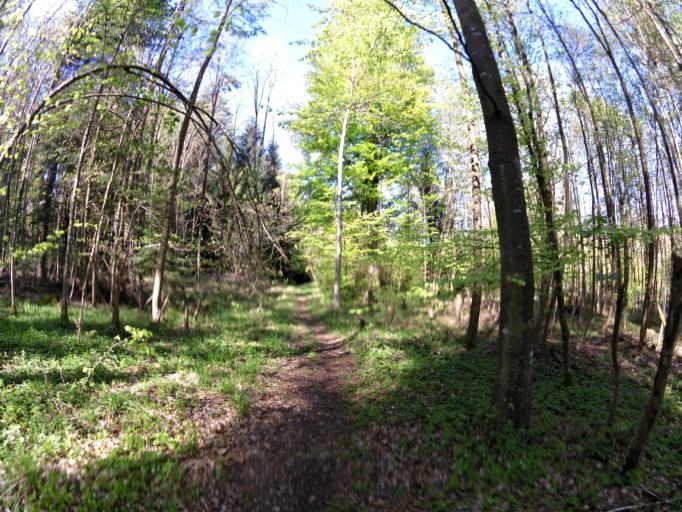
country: CH
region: Aargau
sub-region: Bezirk Aarau
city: Aarau
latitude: 47.4066
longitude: 8.0263
